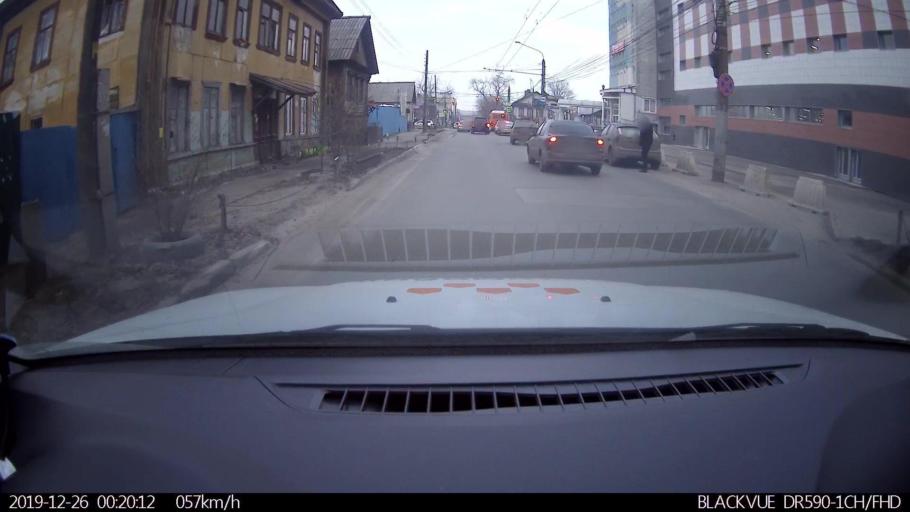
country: RU
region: Nizjnij Novgorod
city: Nizhniy Novgorod
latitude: 56.3161
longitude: 43.9469
